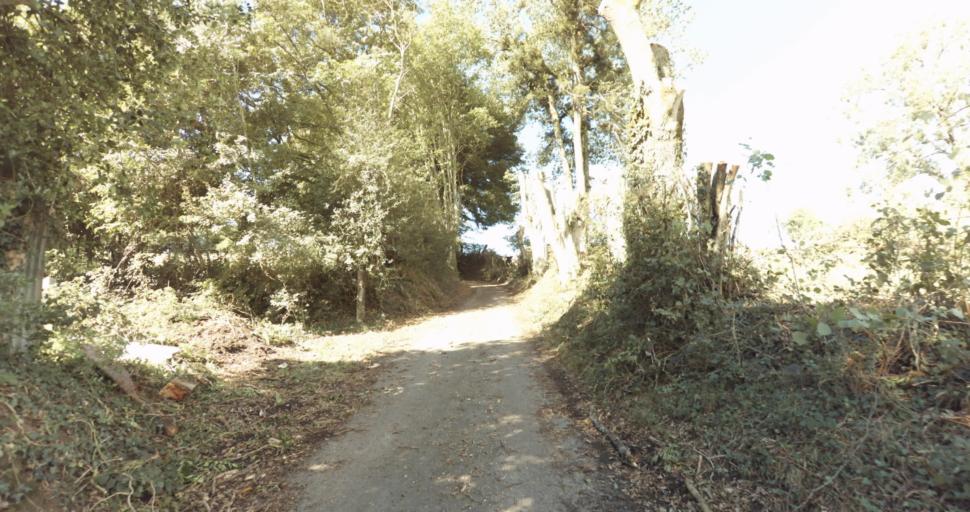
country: FR
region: Lower Normandy
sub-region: Departement de l'Orne
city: Gace
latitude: 48.7973
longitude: 0.2367
